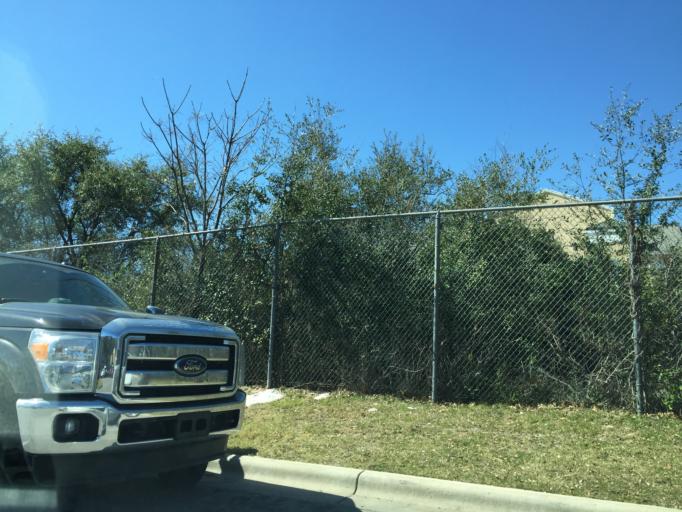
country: US
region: Texas
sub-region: Williamson County
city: Jollyville
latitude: 30.4000
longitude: -97.7281
